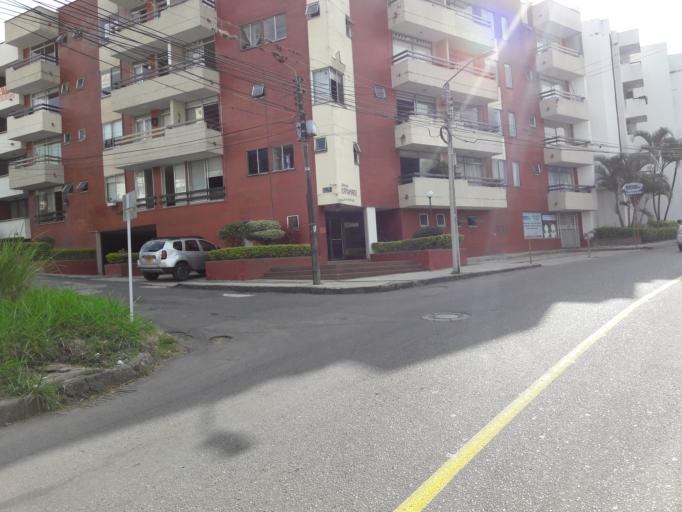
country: CO
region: Tolima
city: Ibague
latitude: 4.4362
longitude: -75.2080
